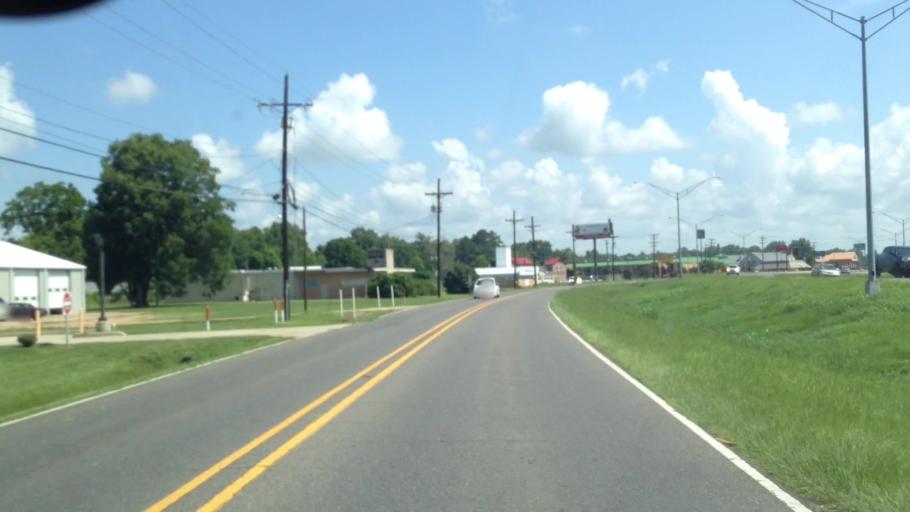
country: US
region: Louisiana
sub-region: Rapides Parish
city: Alexandria
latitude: 31.3072
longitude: -92.4799
